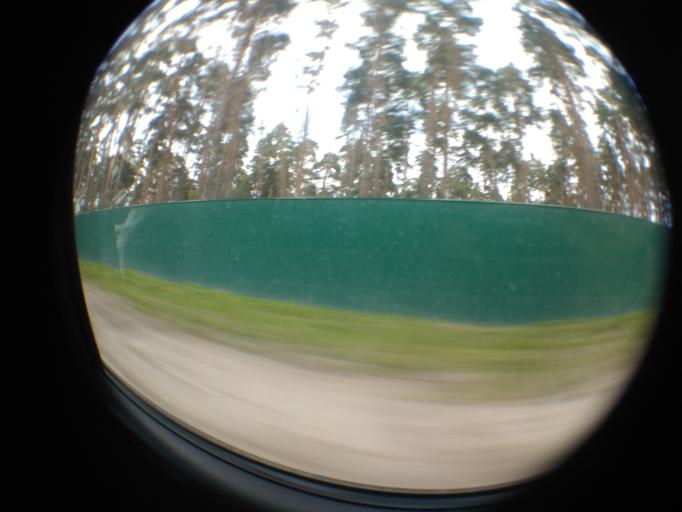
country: RU
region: Moskovskaya
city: Zhukovskiy
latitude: 55.5957
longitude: 38.1389
